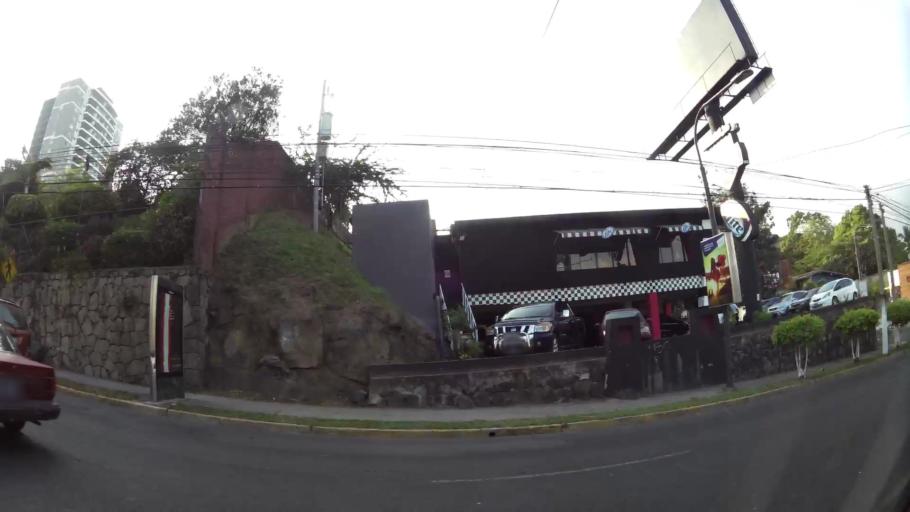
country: SV
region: La Libertad
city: Antiguo Cuscatlan
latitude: 13.6961
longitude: -89.2358
